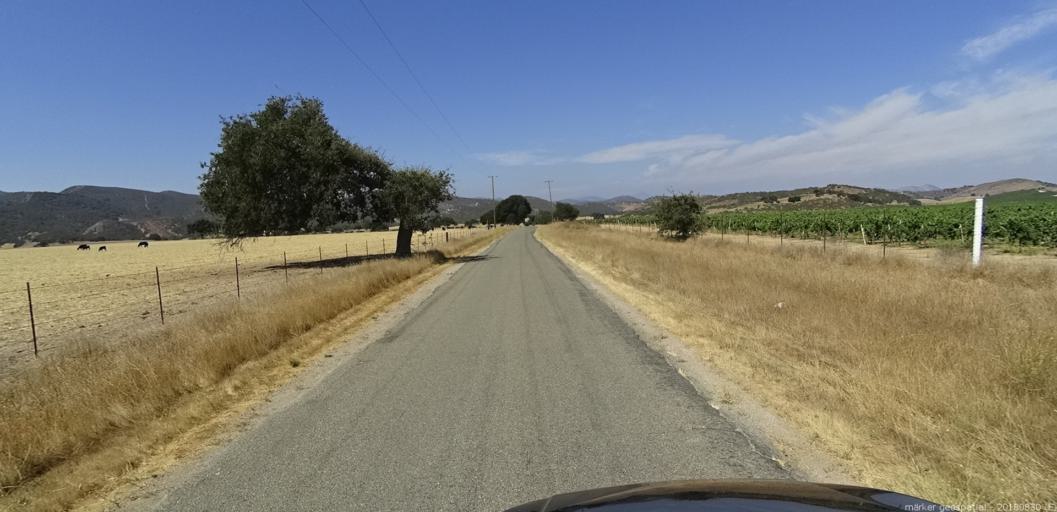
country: US
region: California
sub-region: Monterey County
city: King City
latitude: 36.1109
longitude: -121.0906
